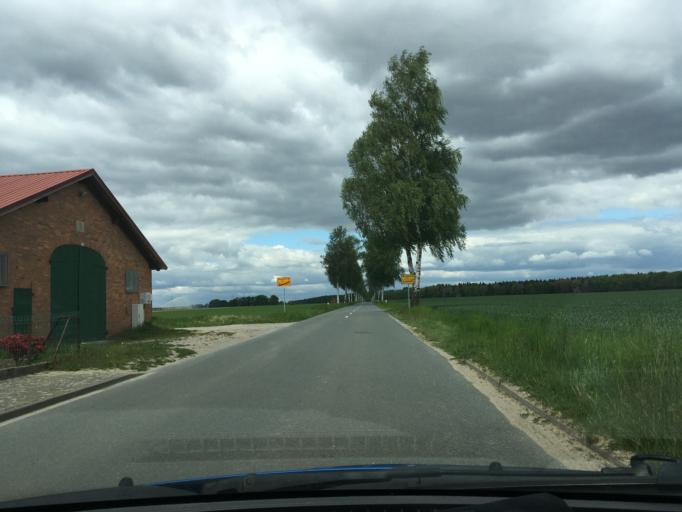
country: DE
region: Lower Saxony
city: Gerdau
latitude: 52.9228
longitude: 10.4139
